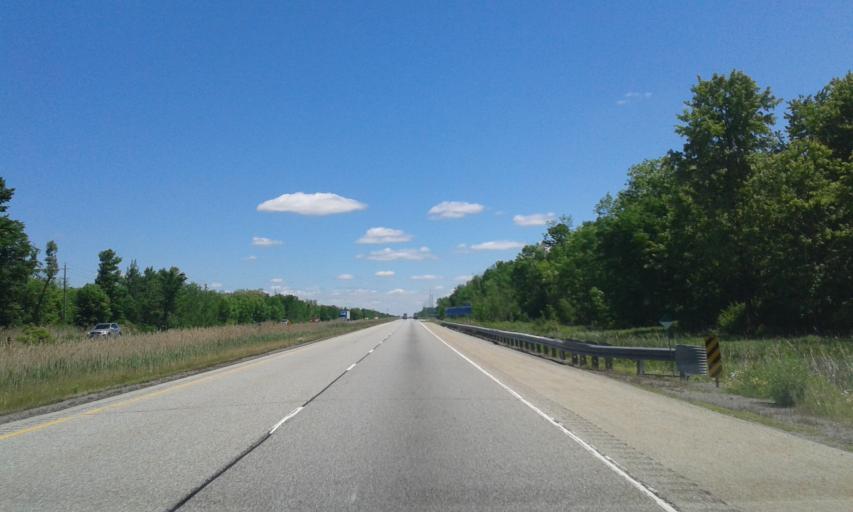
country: US
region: New York
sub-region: St. Lawrence County
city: Norfolk
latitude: 44.9400
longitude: -75.1429
